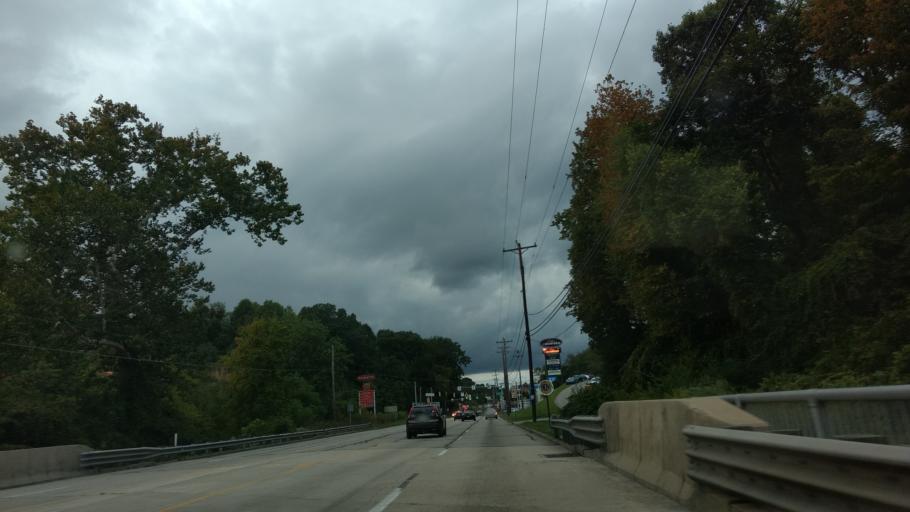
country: US
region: Pennsylvania
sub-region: Allegheny County
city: Pleasant Hills
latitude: 40.3191
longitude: -79.9412
